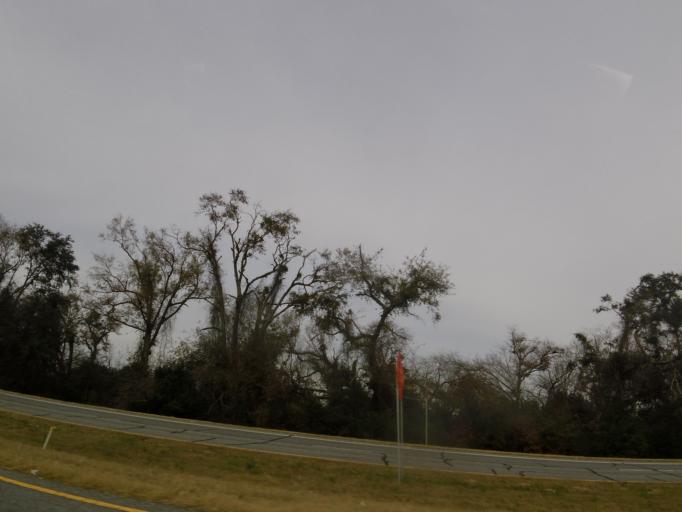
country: US
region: Georgia
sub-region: Seminole County
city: Donalsonville
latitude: 30.9920
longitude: -84.7637
